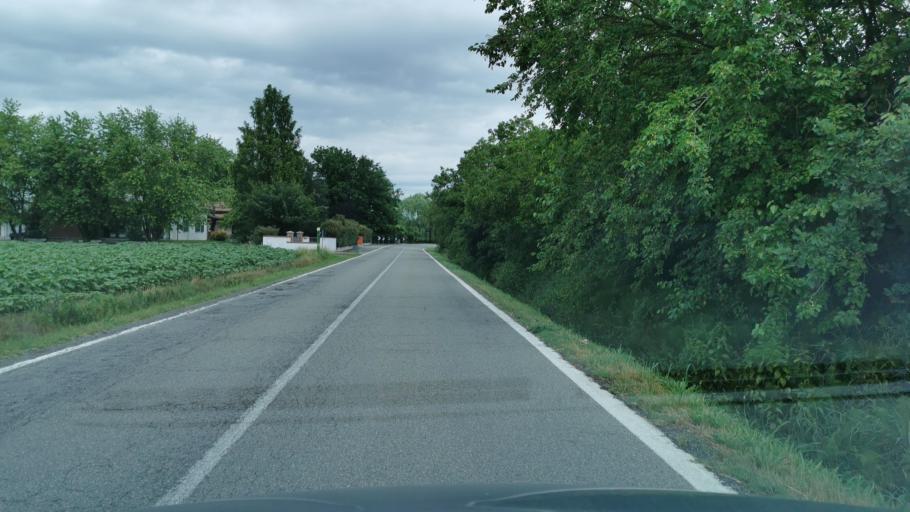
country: IT
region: Emilia-Romagna
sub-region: Provincia di Parma
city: Soragna
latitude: 44.9100
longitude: 10.1031
